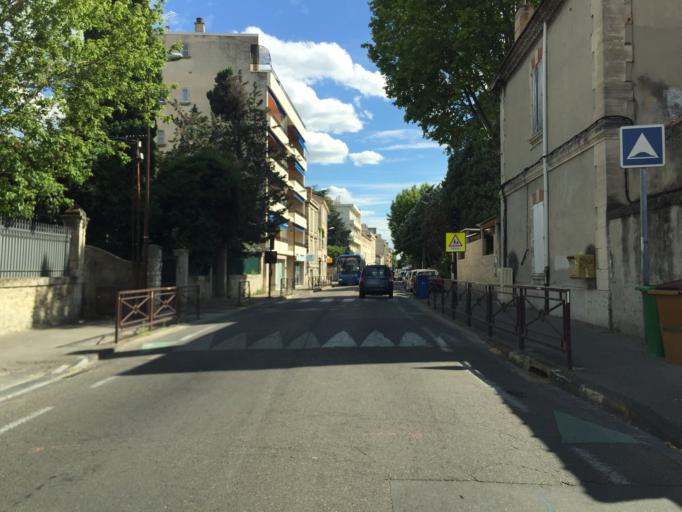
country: FR
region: Provence-Alpes-Cote d'Azur
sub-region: Departement du Vaucluse
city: Avignon
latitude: 43.9393
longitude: 4.8058
